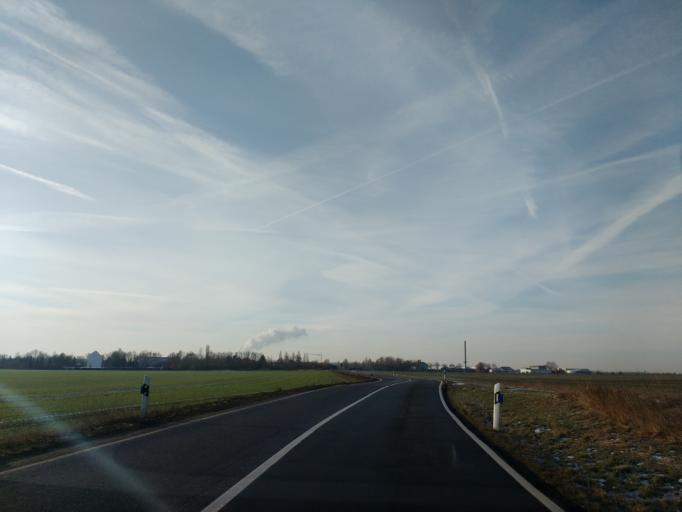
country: DE
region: Saxony-Anhalt
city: Oppin
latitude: 51.5345
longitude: 12.0081
